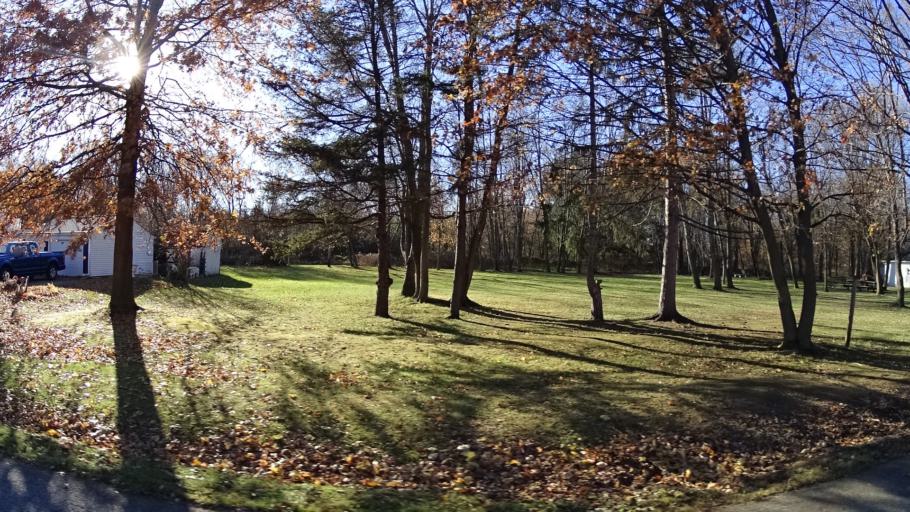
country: US
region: Ohio
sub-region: Lorain County
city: Sheffield
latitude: 41.4178
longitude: -82.1113
